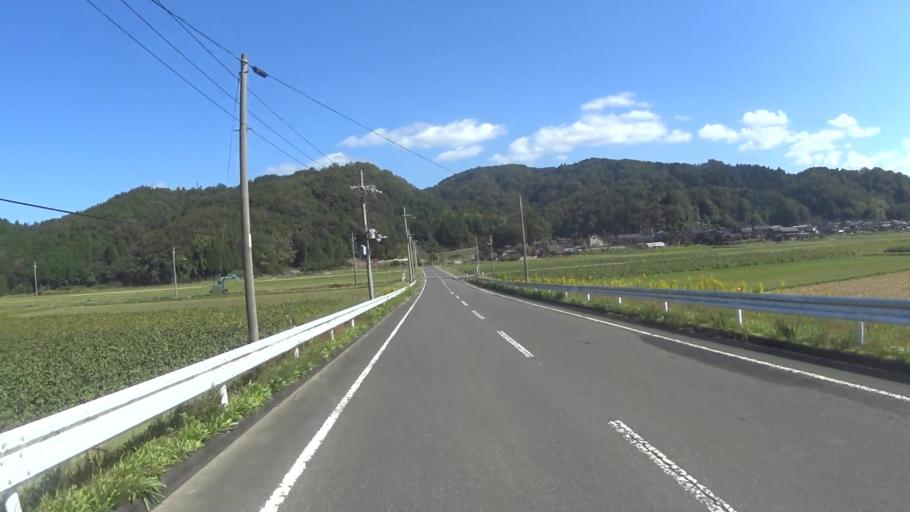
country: JP
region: Hyogo
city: Toyooka
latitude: 35.6004
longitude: 134.9266
